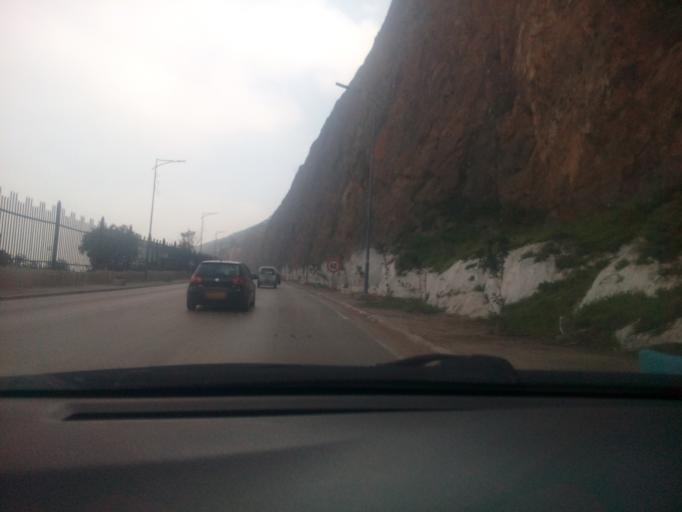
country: DZ
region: Oran
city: Mers el Kebir
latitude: 35.7120
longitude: -0.6816
